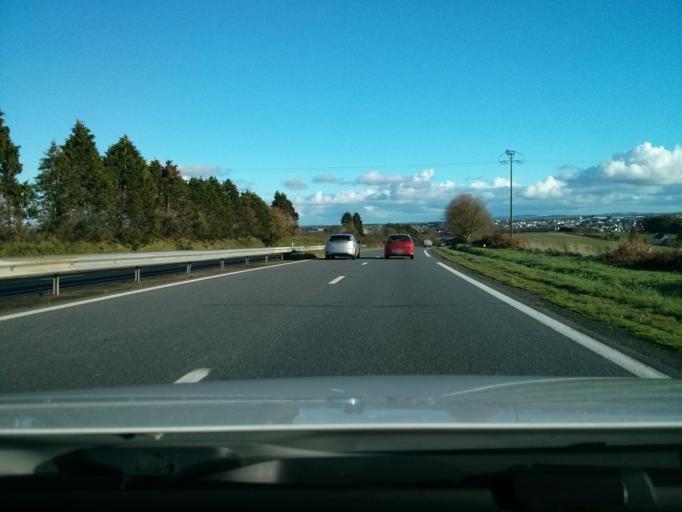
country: FR
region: Brittany
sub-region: Departement du Finistere
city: Guiclan
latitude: 48.5271
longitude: -3.9772
